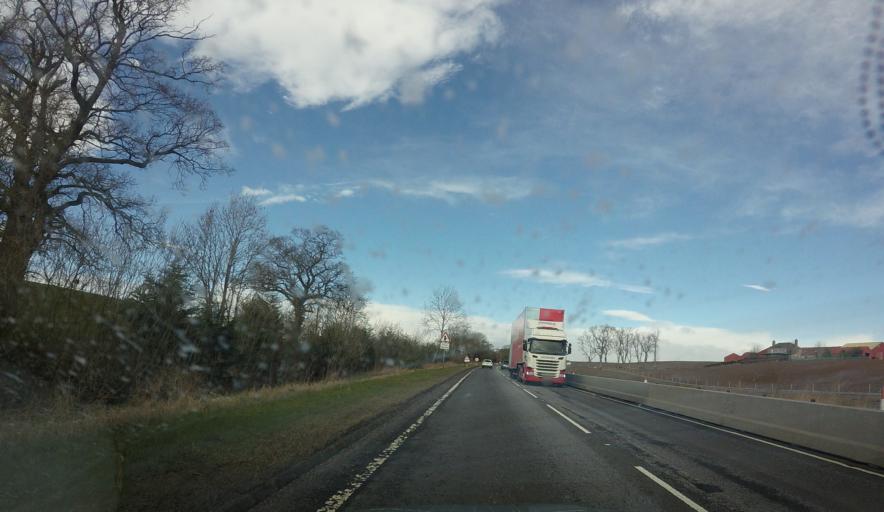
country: GB
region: Scotland
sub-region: Perth and Kinross
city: Bankfoot
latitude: 56.4804
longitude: -3.4939
